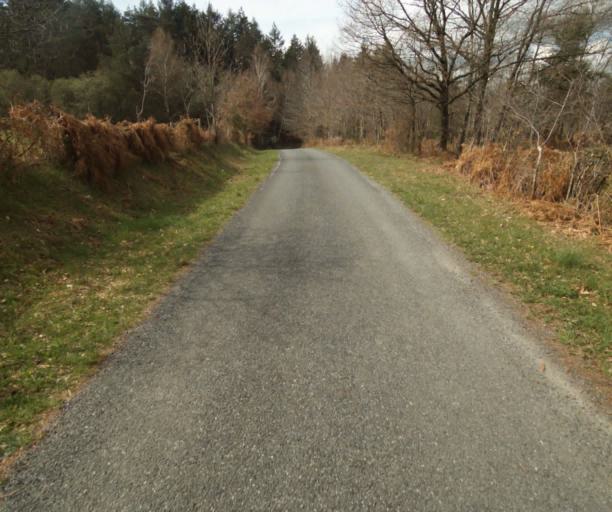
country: FR
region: Limousin
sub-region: Departement de la Correze
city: Correze
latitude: 45.3821
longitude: 1.9181
